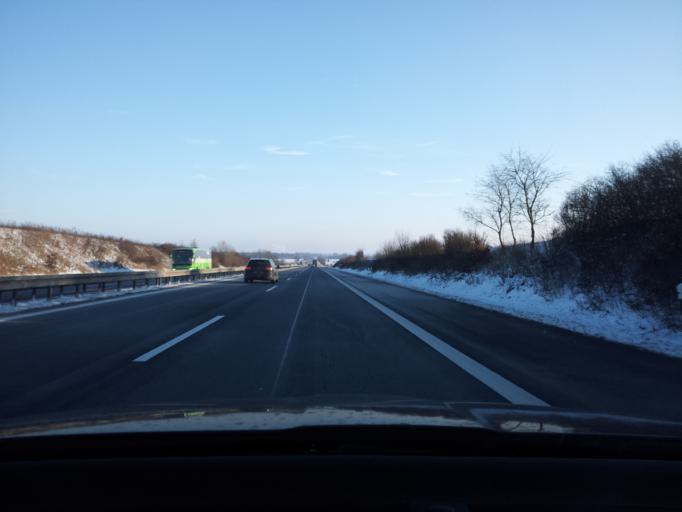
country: DE
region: Brandenburg
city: Gerdshagen
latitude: 53.2171
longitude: 12.2391
